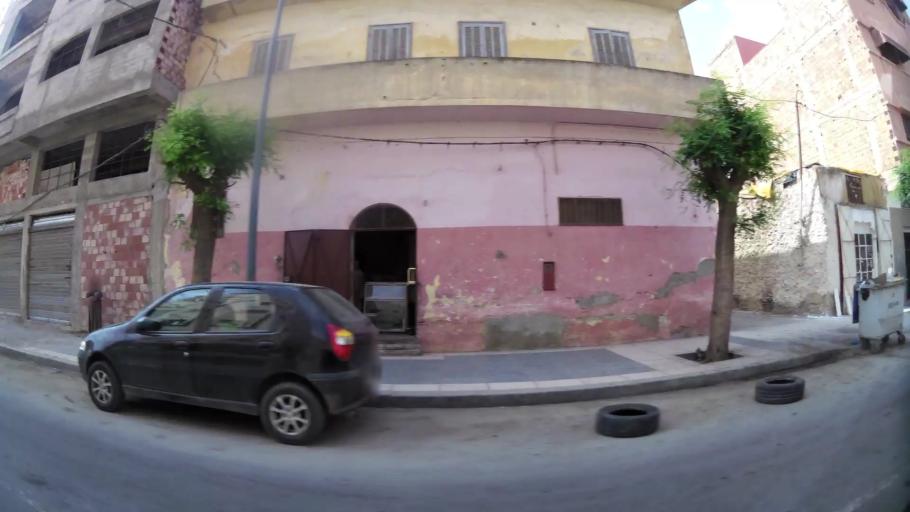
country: MA
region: Oriental
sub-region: Oujda-Angad
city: Oujda
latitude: 34.6849
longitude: -1.9107
